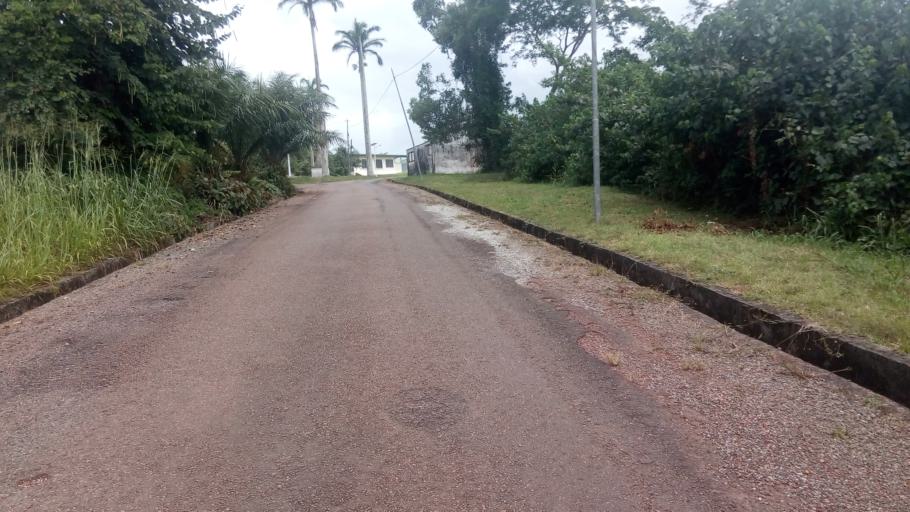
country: GH
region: Western
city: Tarkwa
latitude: 5.2956
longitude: -2.0112
